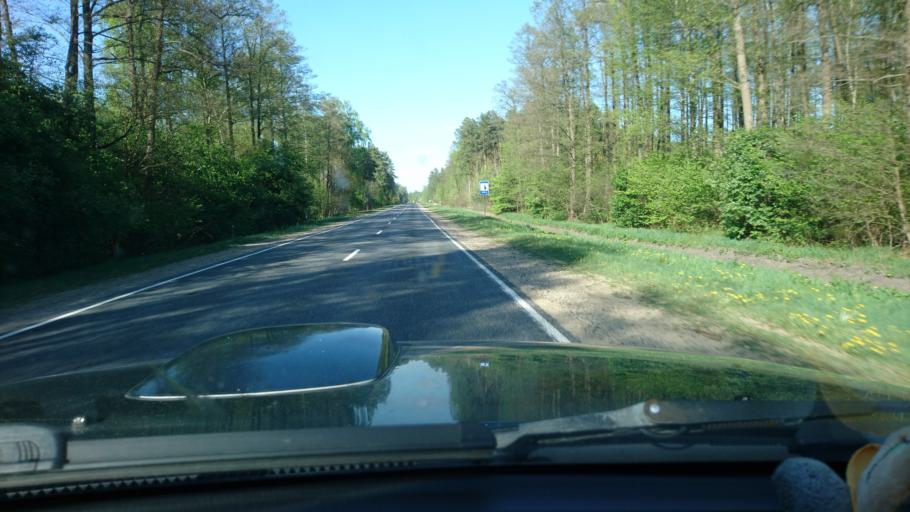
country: BY
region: Brest
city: Zhabinka
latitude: 52.3939
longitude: 24.1750
